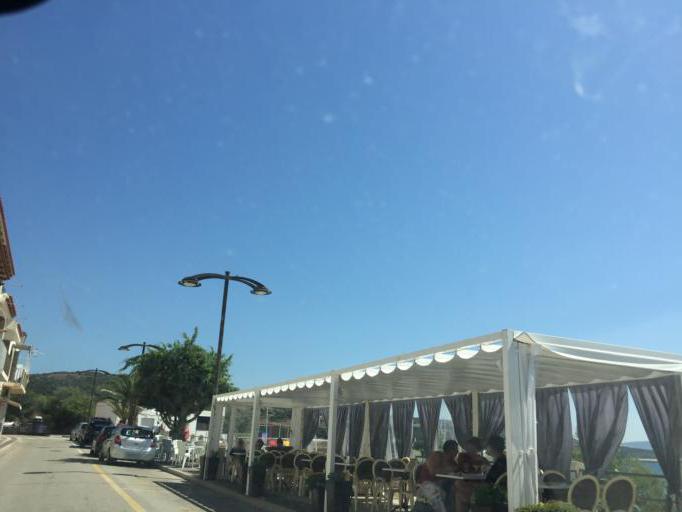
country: IT
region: Sardinia
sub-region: Provincia di Olbia-Tempio
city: Trinita d'Agultu
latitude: 41.0127
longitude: 8.8747
